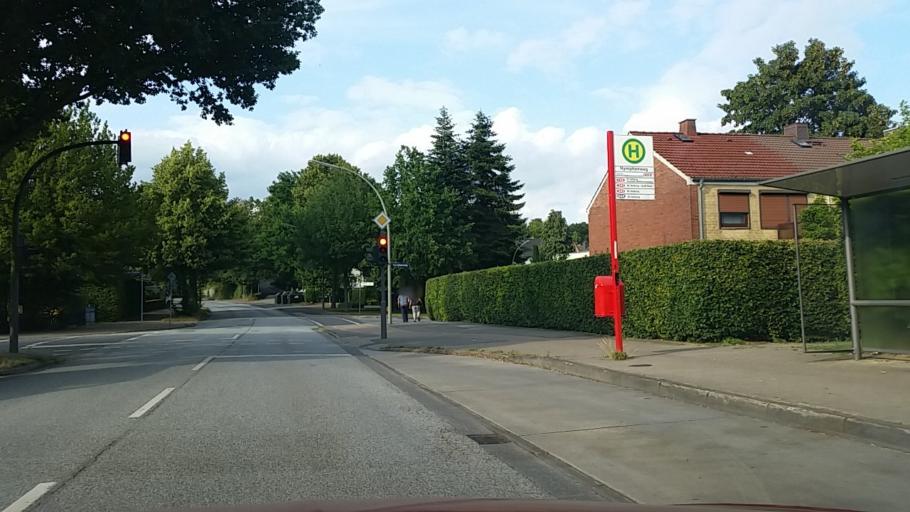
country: DE
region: Hamburg
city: Harburg
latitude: 53.4419
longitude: 9.9685
